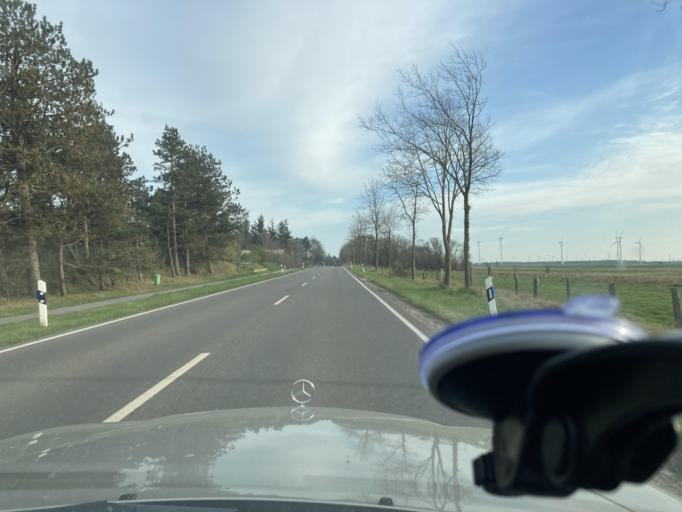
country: DE
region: Schleswig-Holstein
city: Stelle-Wittenwurth
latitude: 54.2794
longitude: 9.0458
